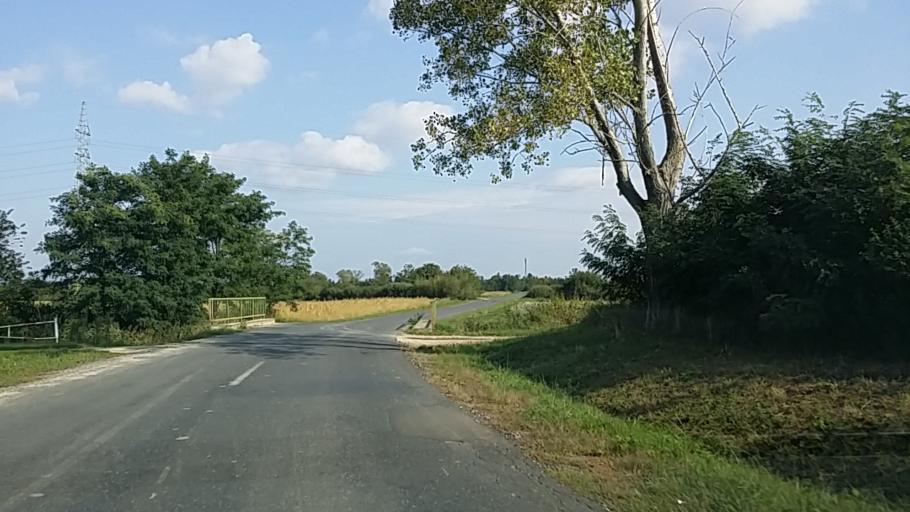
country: HU
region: Vas
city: Csepreg
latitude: 47.3838
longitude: 16.7148
